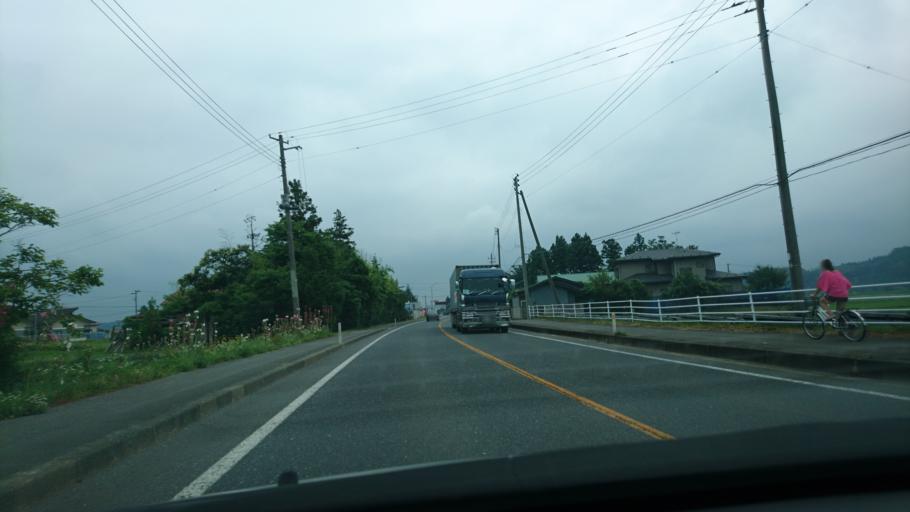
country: JP
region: Miyagi
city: Furukawa
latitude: 38.6831
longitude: 140.8566
